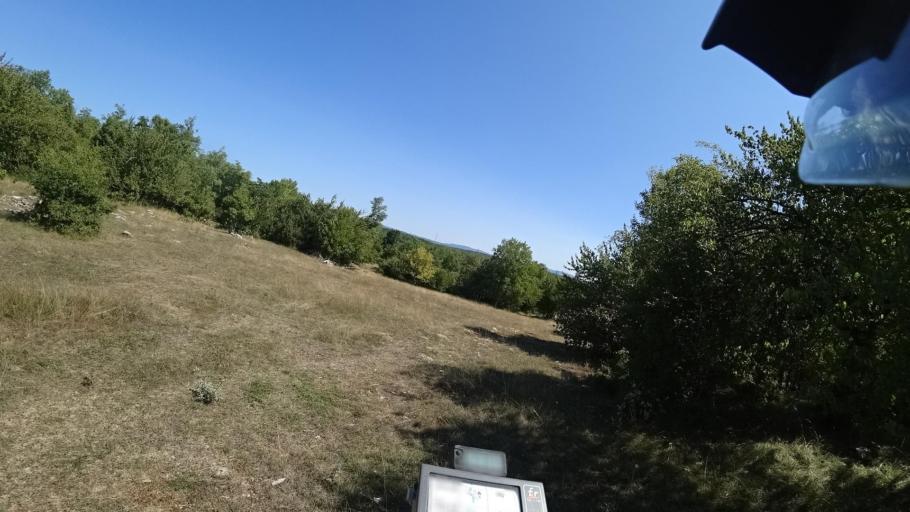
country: HR
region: Licko-Senjska
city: Otocac
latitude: 44.7339
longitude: 15.3528
